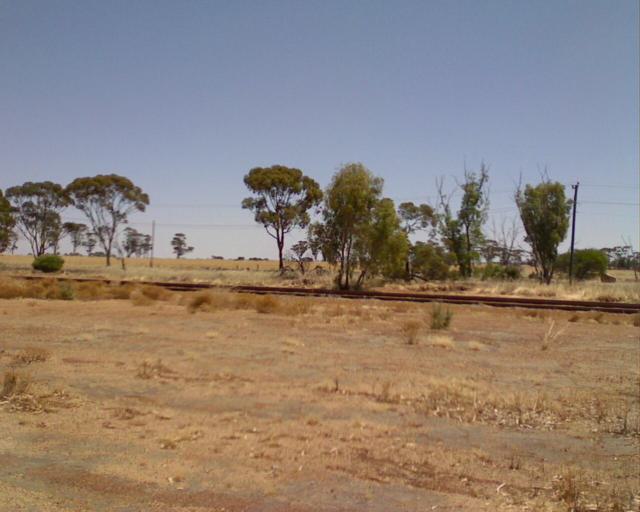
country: AU
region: Western Australia
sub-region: Wongan-Ballidu
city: Wongan Hills
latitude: -30.4551
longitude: 117.5270
